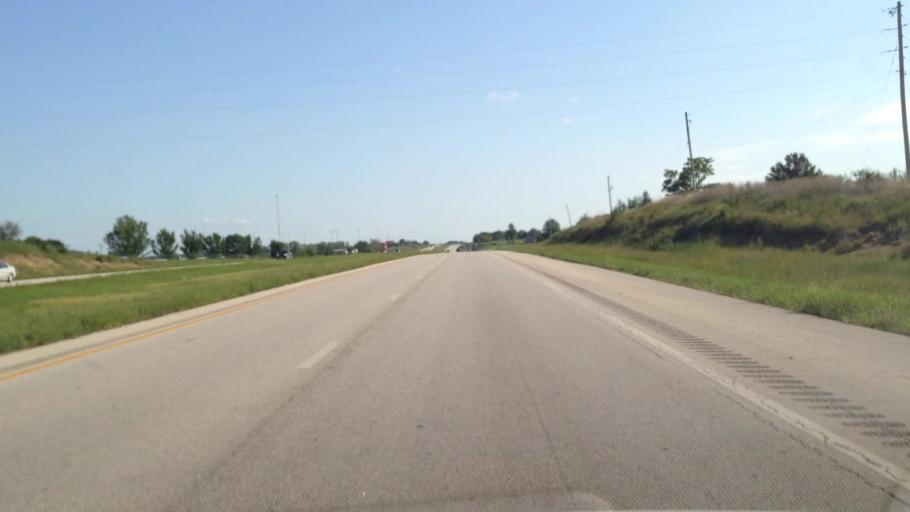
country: US
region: Kansas
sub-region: Bourbon County
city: Fort Scott
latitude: 37.7975
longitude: -94.7051
